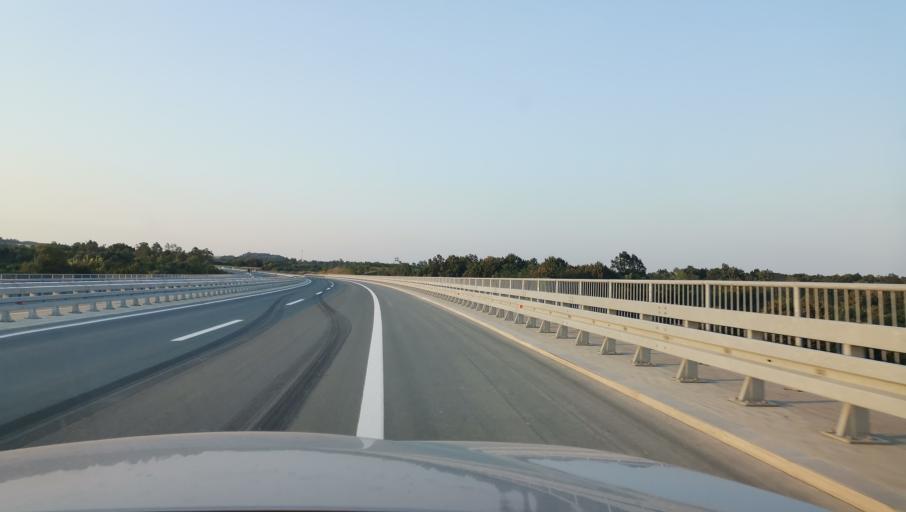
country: RS
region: Central Serbia
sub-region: Kolubarski Okrug
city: Ub
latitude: 44.4173
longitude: 20.1048
